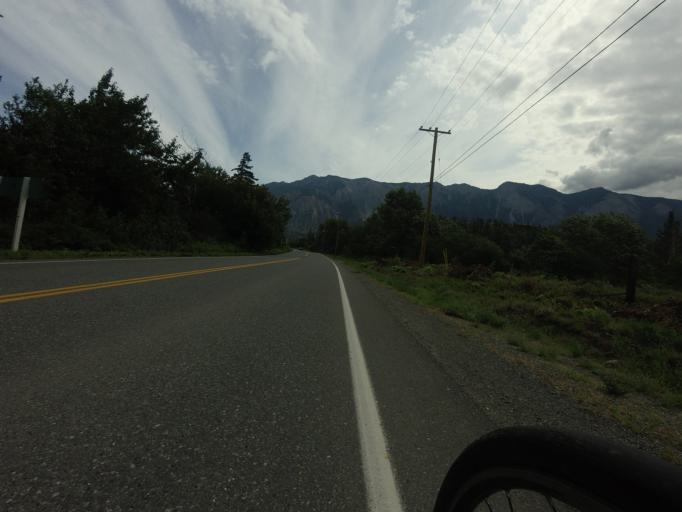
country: CA
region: British Columbia
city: Lillooet
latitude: 50.6738
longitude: -121.9358
